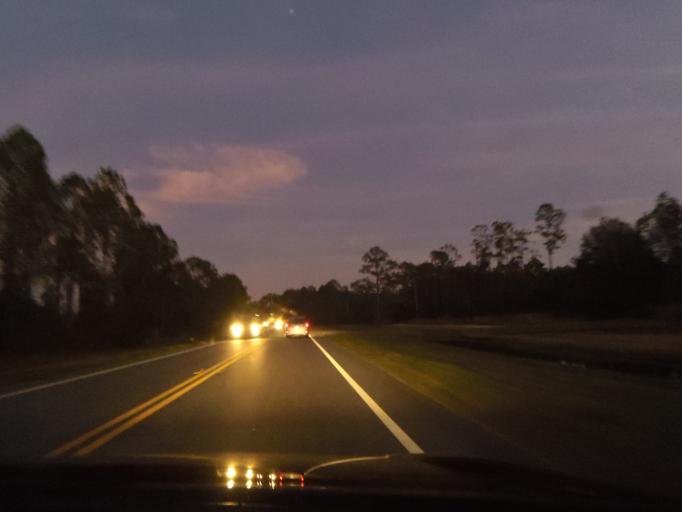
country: US
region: Florida
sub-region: Volusia County
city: De Leon Springs
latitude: 29.2395
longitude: -81.2360
